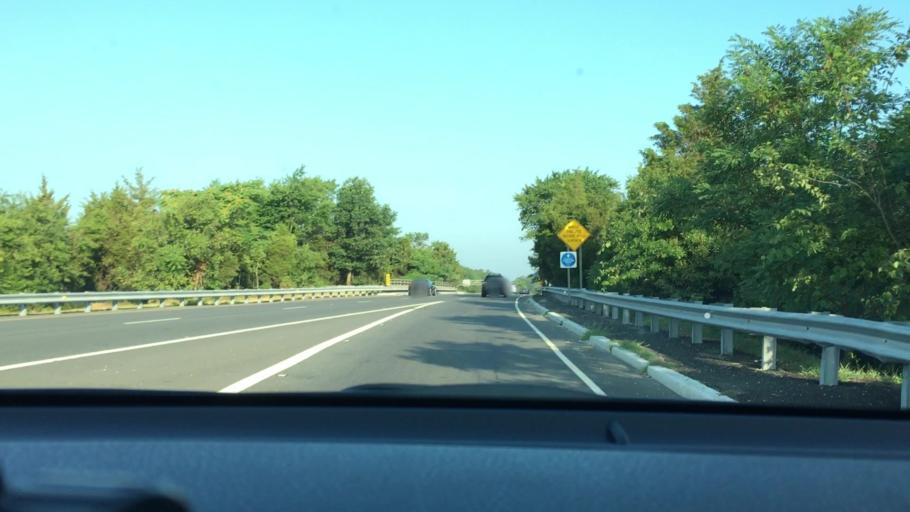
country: US
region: New Jersey
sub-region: Cumberland County
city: South Vineland
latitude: 39.4282
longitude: -75.0390
